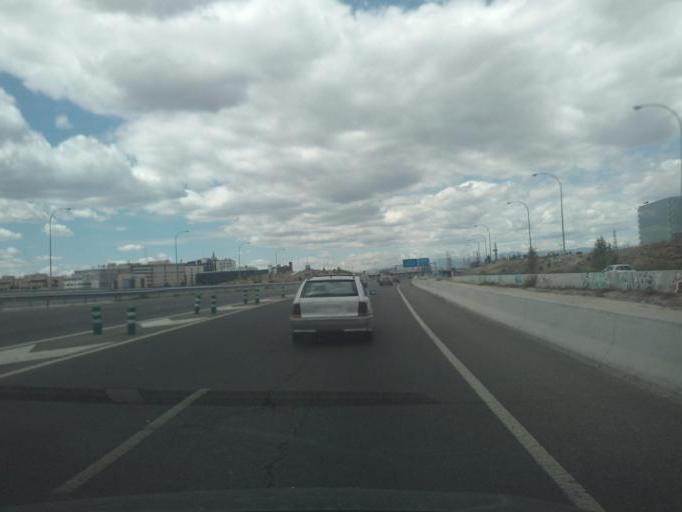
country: ES
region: Madrid
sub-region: Provincia de Madrid
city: Las Tablas
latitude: 40.5106
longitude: -3.6640
